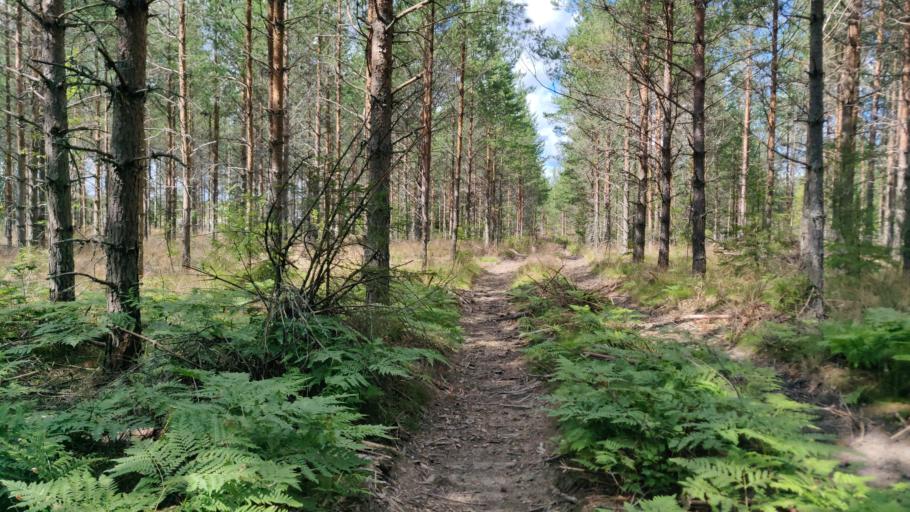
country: SE
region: Vaermland
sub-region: Hagfors Kommun
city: Hagfors
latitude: 60.0267
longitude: 13.5838
